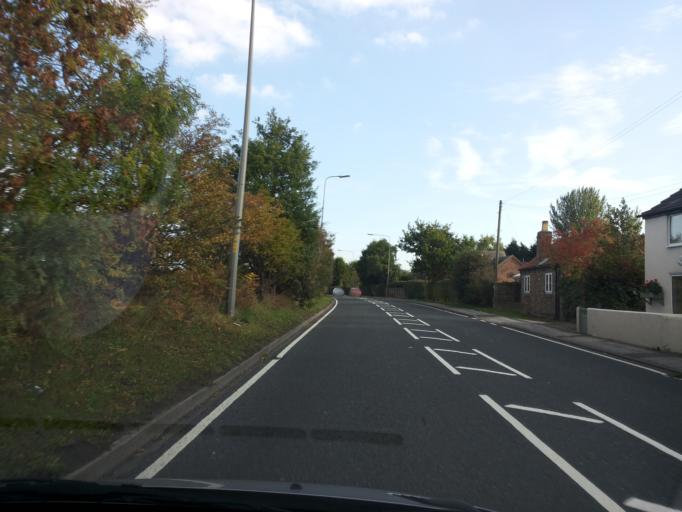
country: GB
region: England
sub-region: North Yorkshire
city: Camblesforth
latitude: 53.7286
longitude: -1.0318
